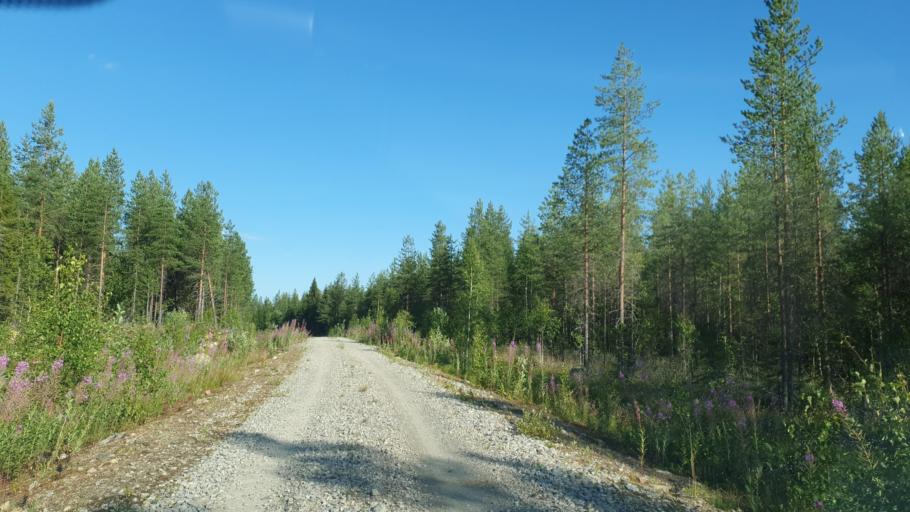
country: FI
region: Kainuu
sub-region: Kehys-Kainuu
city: Kuhmo
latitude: 64.0028
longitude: 29.7652
